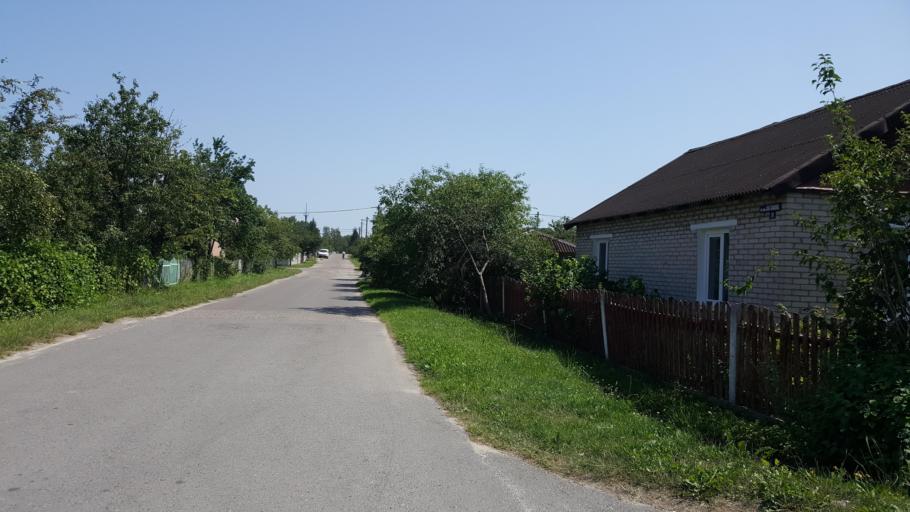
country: BY
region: Brest
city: Zhabinka
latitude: 52.1942
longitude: 24.0131
